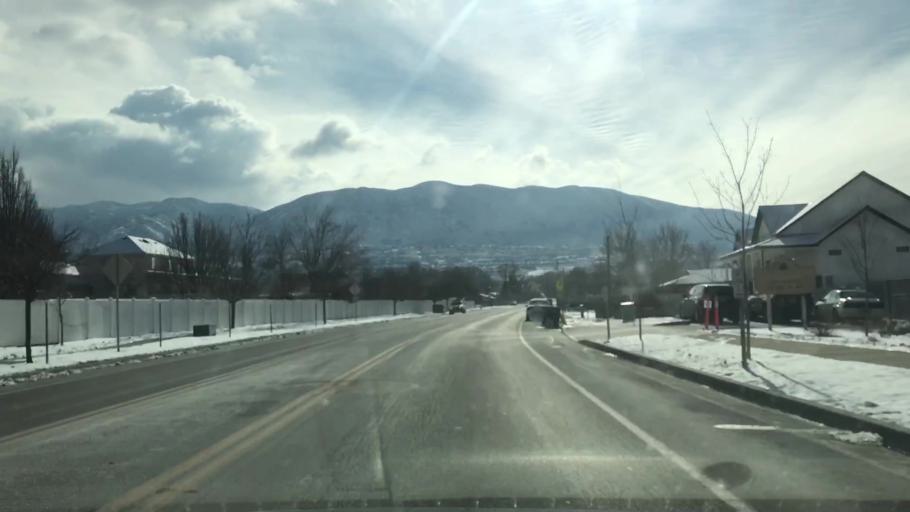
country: US
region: Utah
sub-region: Salt Lake County
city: Draper
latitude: 40.5074
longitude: -111.8819
